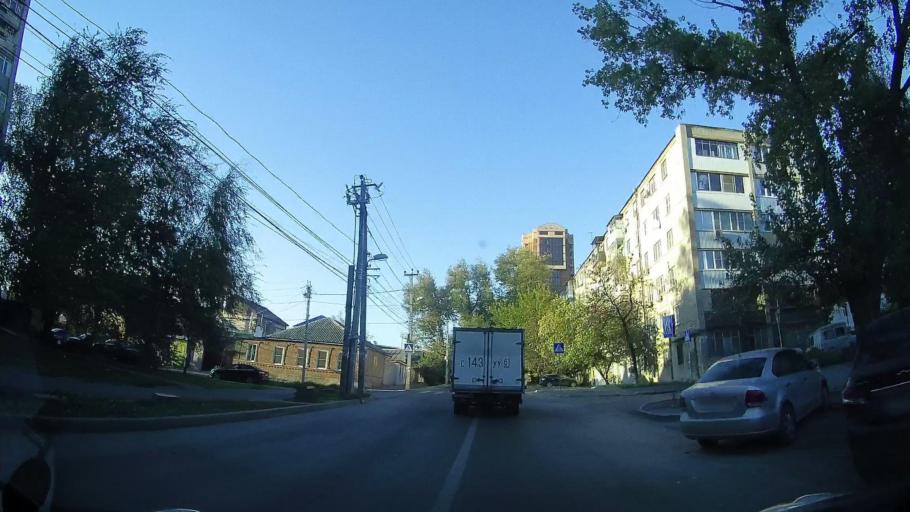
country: RU
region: Rostov
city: Rostov-na-Donu
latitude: 47.2328
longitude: 39.6923
